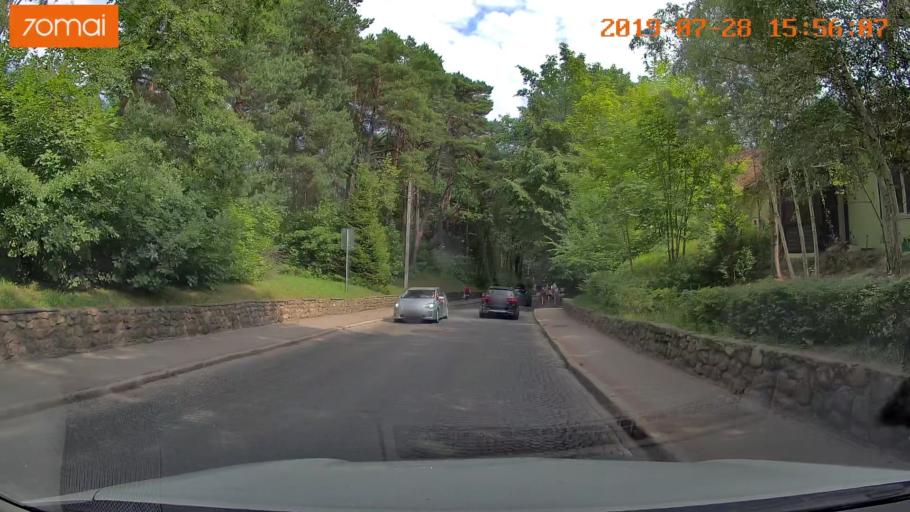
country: RU
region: Kaliningrad
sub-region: Gorod Svetlogorsk
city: Svetlogorsk
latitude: 54.9402
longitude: 20.1443
